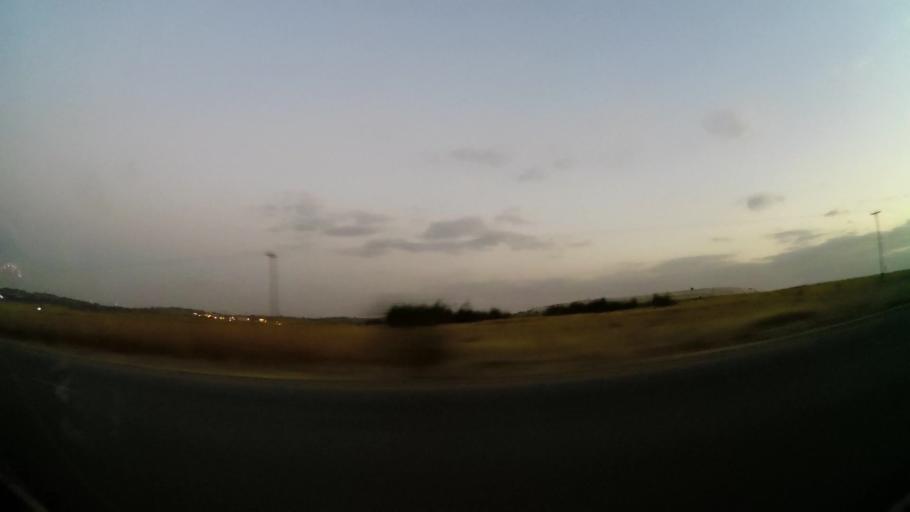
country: ZA
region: Gauteng
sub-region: West Rand District Municipality
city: Krugersdorp
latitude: -26.1101
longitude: 27.7115
